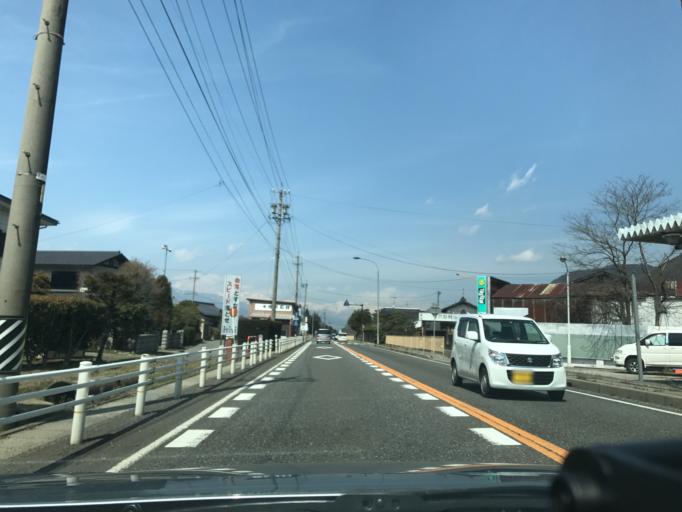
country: JP
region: Nagano
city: Toyoshina
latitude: 36.2928
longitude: 137.9432
